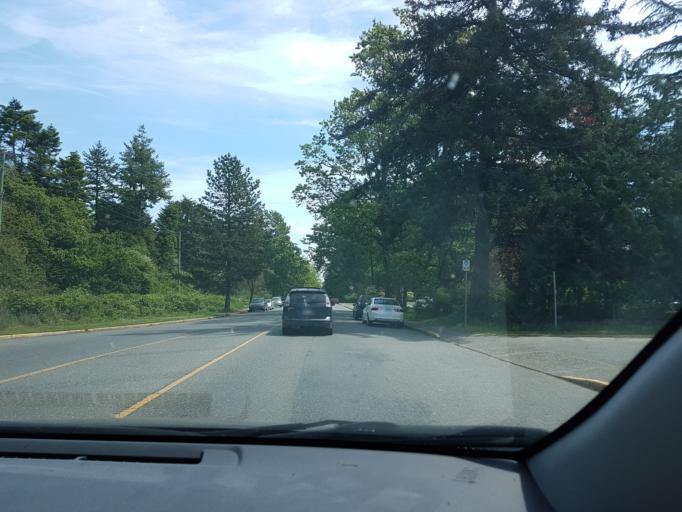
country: CA
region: British Columbia
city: Oak Bay
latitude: 48.4587
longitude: -123.3152
